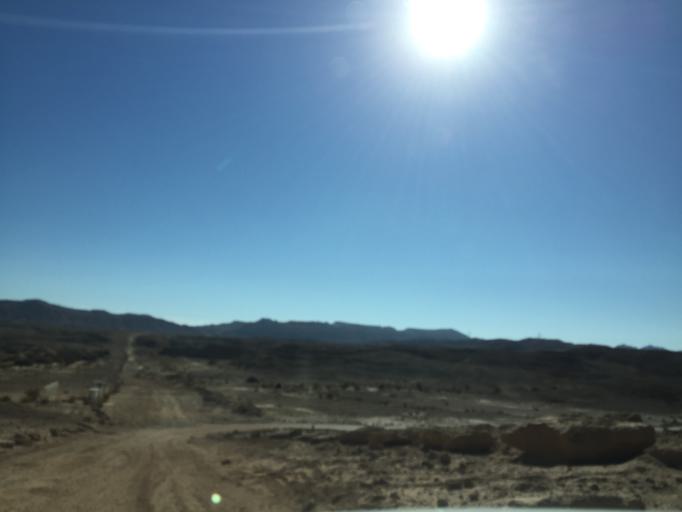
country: IL
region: Southern District
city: Mitzpe Ramon
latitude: 30.6190
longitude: 34.9201
